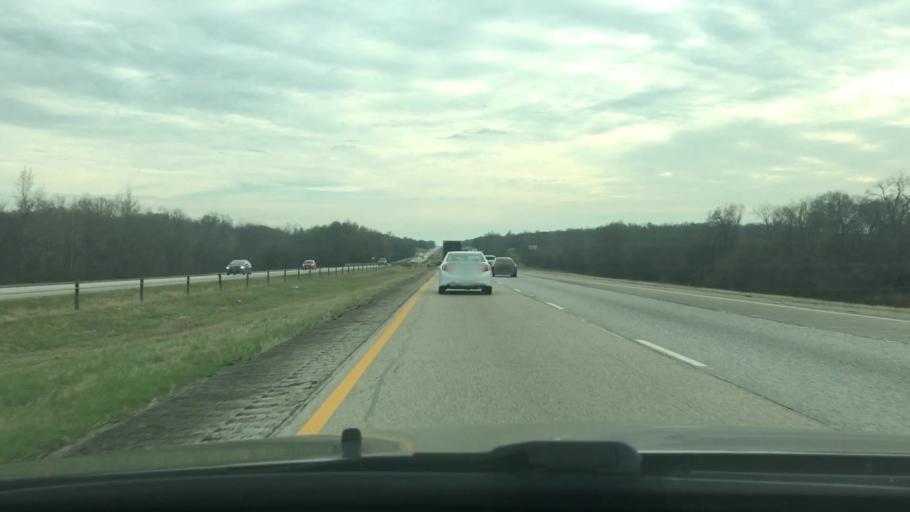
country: US
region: Texas
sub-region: Leon County
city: Centerville
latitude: 31.1913
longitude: -95.9927
